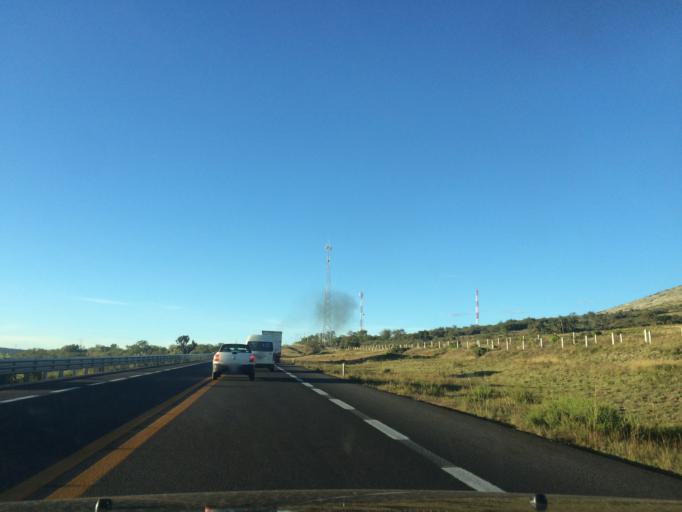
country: MX
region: Puebla
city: Morelos Canada
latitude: 18.7181
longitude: -97.4717
